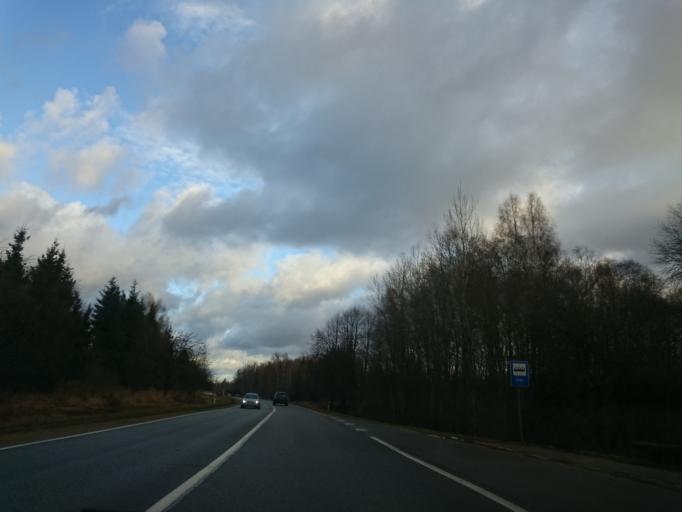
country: LV
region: Ligatne
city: Ligatne
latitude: 57.1697
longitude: 24.9701
